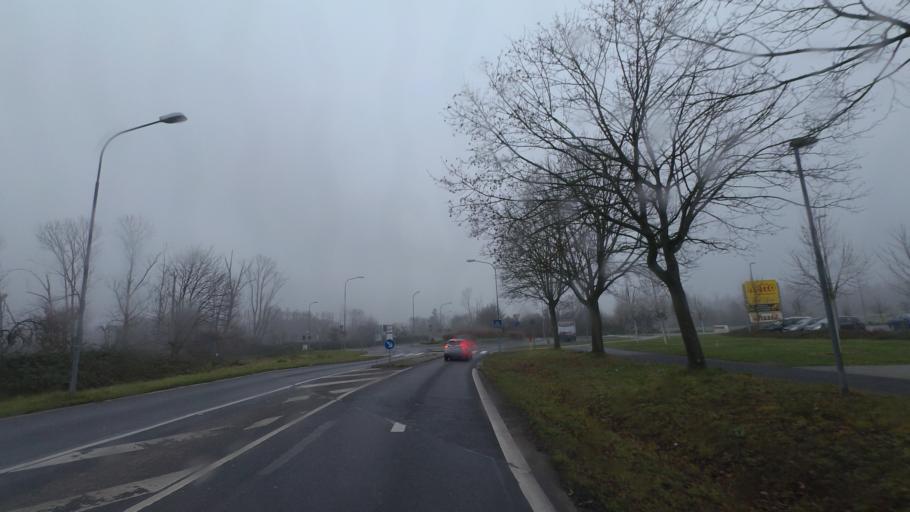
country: DE
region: Hesse
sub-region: Regierungsbezirk Darmstadt
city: Seligenstadt
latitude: 50.0524
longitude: 8.9454
